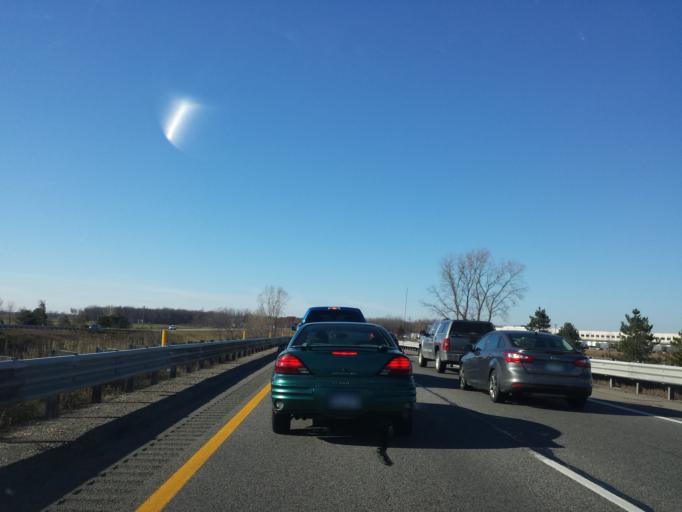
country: US
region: Michigan
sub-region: Ingham County
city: Webberville
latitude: 42.6599
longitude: -84.1991
